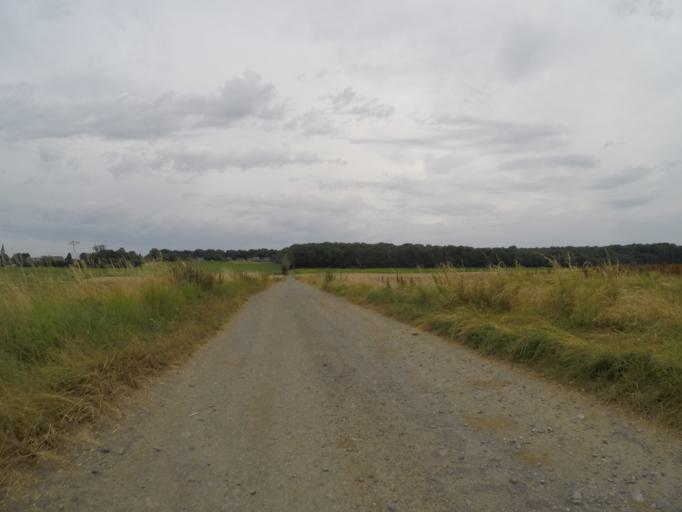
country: BE
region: Wallonia
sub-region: Province de Namur
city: Assesse
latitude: 50.2961
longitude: 5.0227
